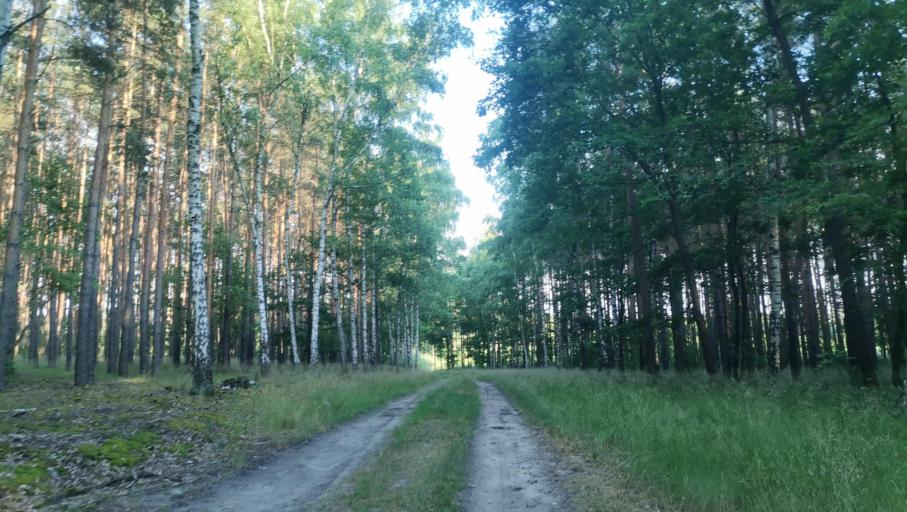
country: PL
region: Greater Poland Voivodeship
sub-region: Powiat jarocinski
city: Witaszyce
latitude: 51.9800
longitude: 17.5456
